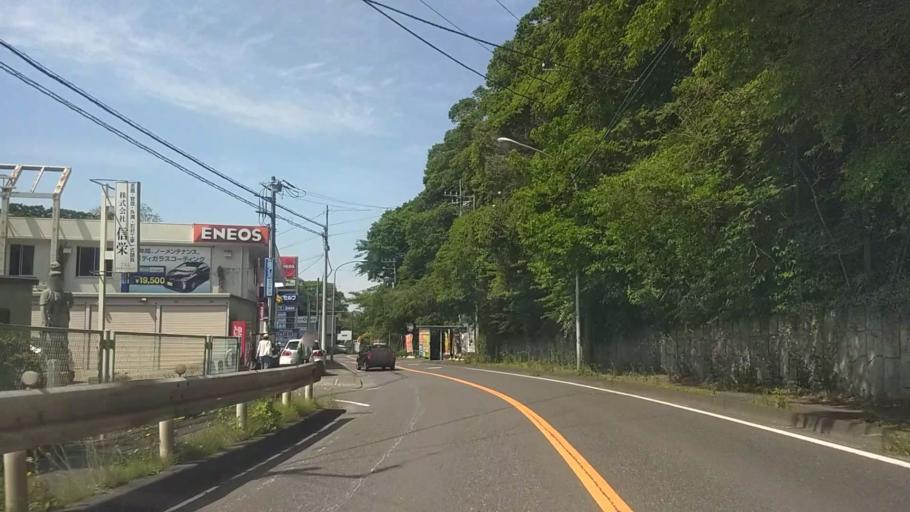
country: JP
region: Kanagawa
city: Kamakura
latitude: 35.3424
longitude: 139.5820
